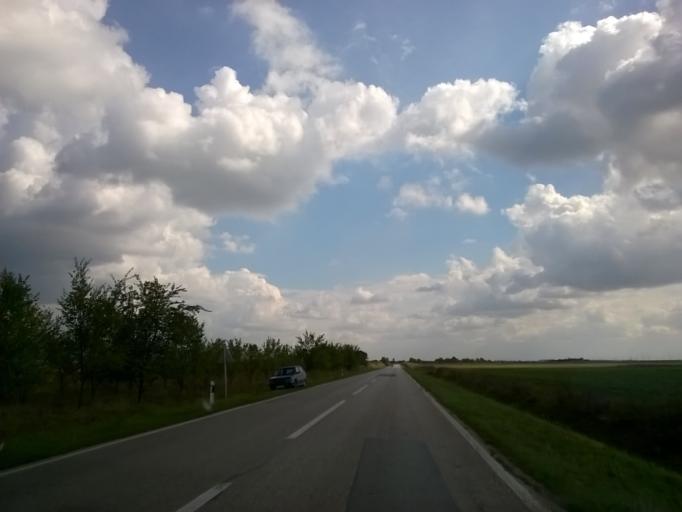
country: RS
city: Pavlis
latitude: 45.1528
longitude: 21.2554
